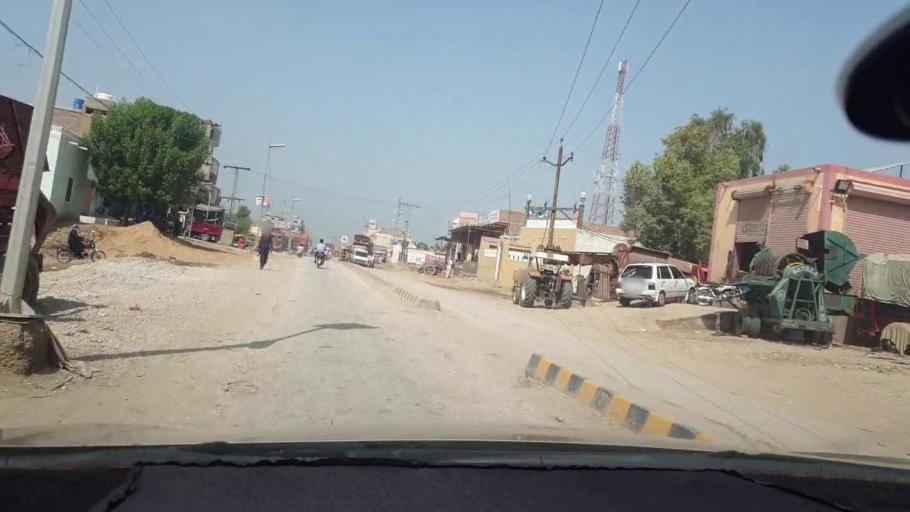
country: PK
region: Sindh
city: Kambar
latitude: 27.5891
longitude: 68.0126
